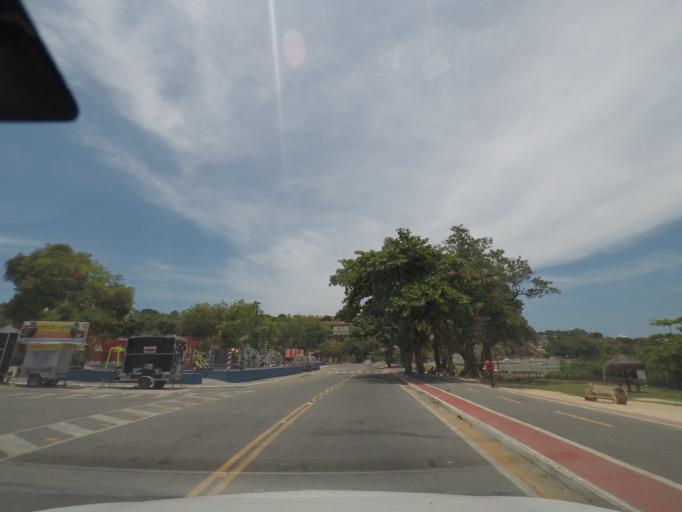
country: BR
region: Rio de Janeiro
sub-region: Marica
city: Marica
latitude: -22.9275
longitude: -42.8266
